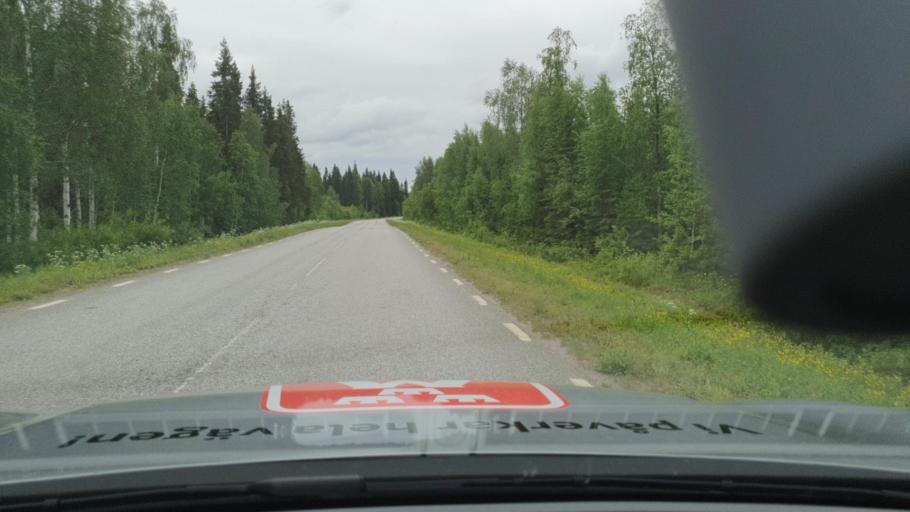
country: SE
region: Norrbotten
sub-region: Lulea Kommun
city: Ranea
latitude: 65.8637
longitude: 22.2335
